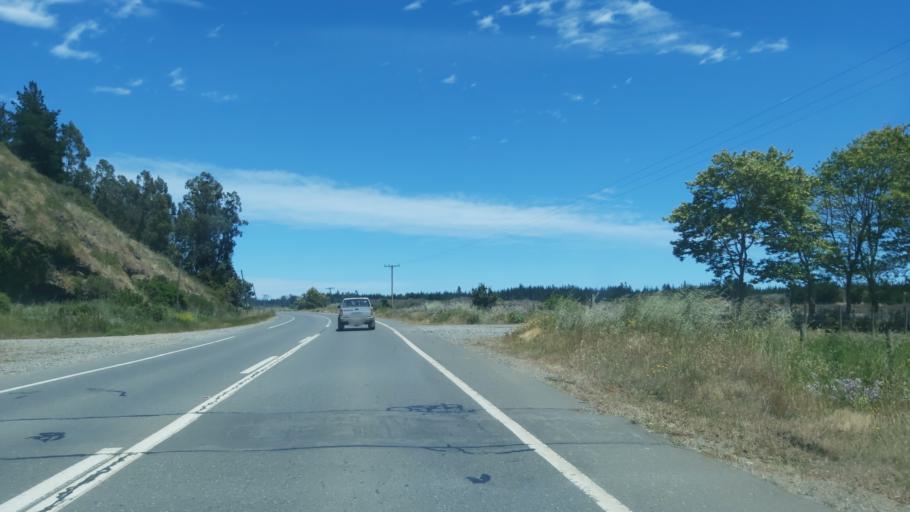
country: CL
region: Maule
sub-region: Provincia de Talca
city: Constitucion
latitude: -35.2806
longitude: -72.3574
